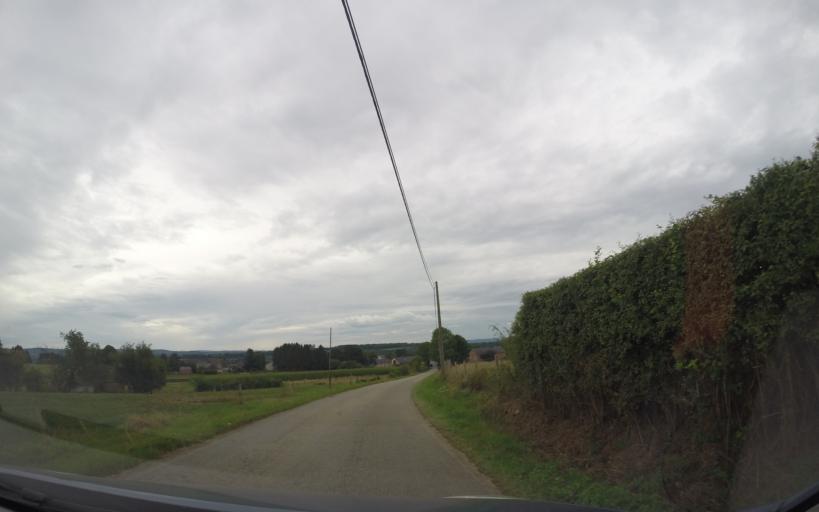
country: BE
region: Wallonia
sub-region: Province du Luxembourg
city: Durbuy
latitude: 50.3680
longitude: 5.4660
